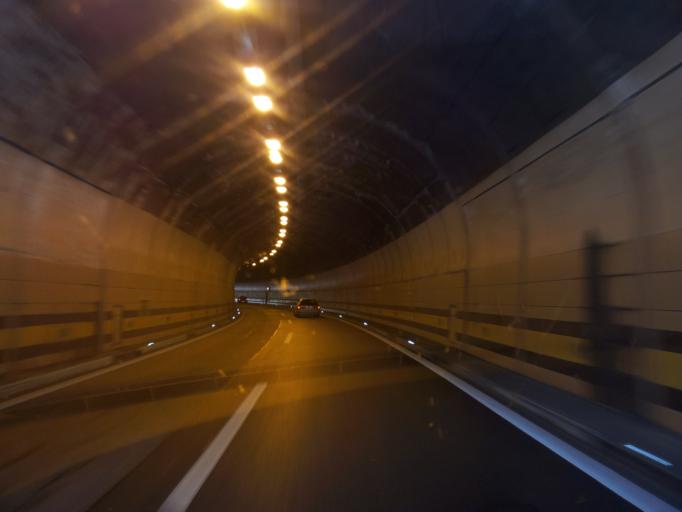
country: CH
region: Uri
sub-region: Uri
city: Silenen
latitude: 46.7662
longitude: 8.6618
